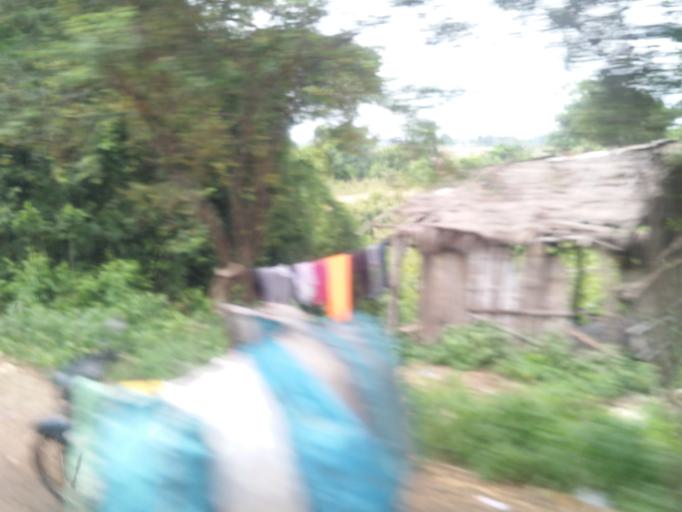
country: KH
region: Kratie
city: Kratie
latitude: 12.2037
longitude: 105.9447
